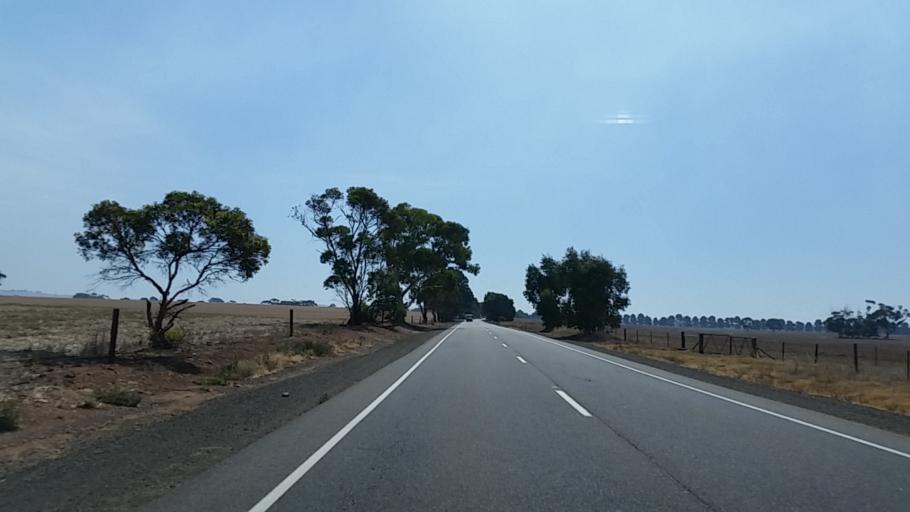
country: AU
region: South Australia
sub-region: Light
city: Kapunda
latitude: -34.2448
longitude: 138.7472
